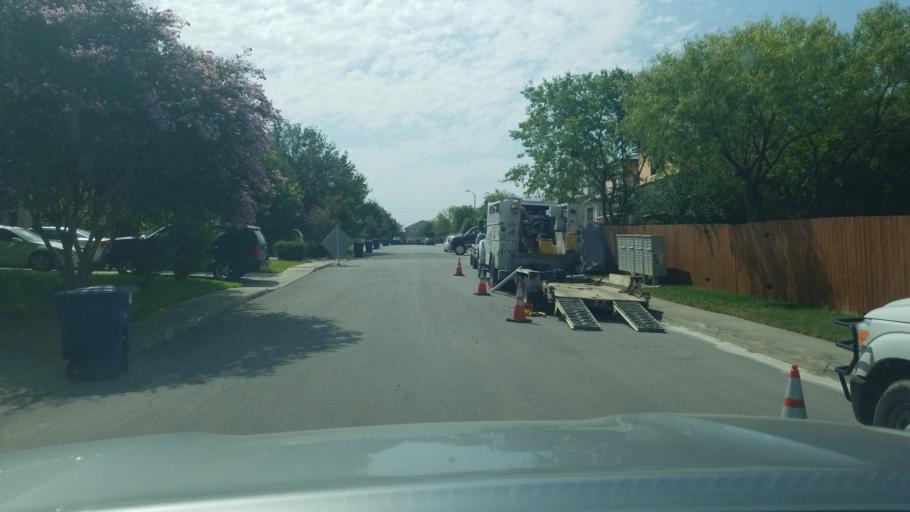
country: US
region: Texas
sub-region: Bexar County
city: Castle Hills
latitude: 29.5457
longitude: -98.5173
